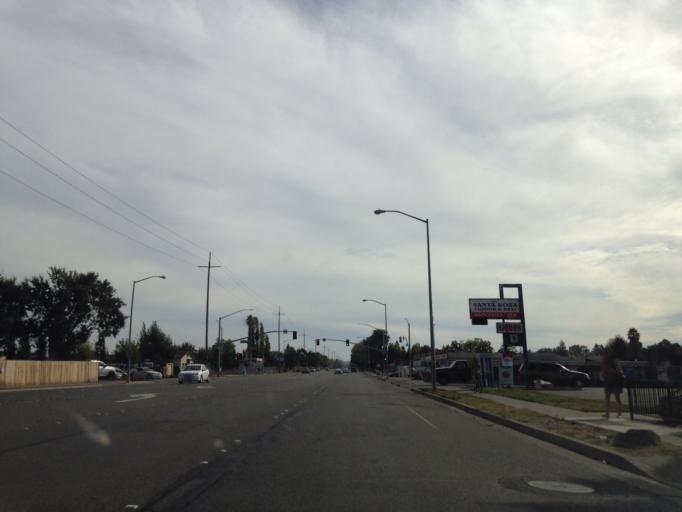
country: US
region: California
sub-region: Sonoma County
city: Roseland
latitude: 38.3956
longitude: -122.7136
